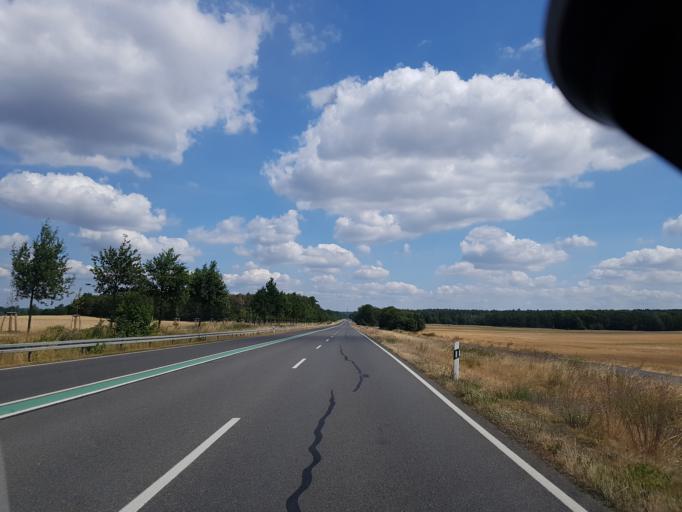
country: DE
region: Brandenburg
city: Drebkau
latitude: 51.6682
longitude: 14.2444
